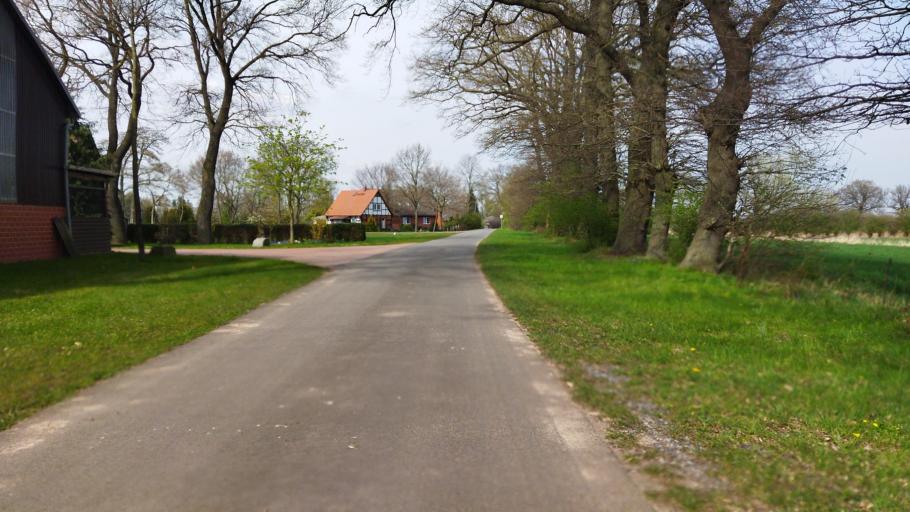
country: DE
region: Lower Saxony
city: Raddestorf
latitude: 52.4373
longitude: 8.9828
